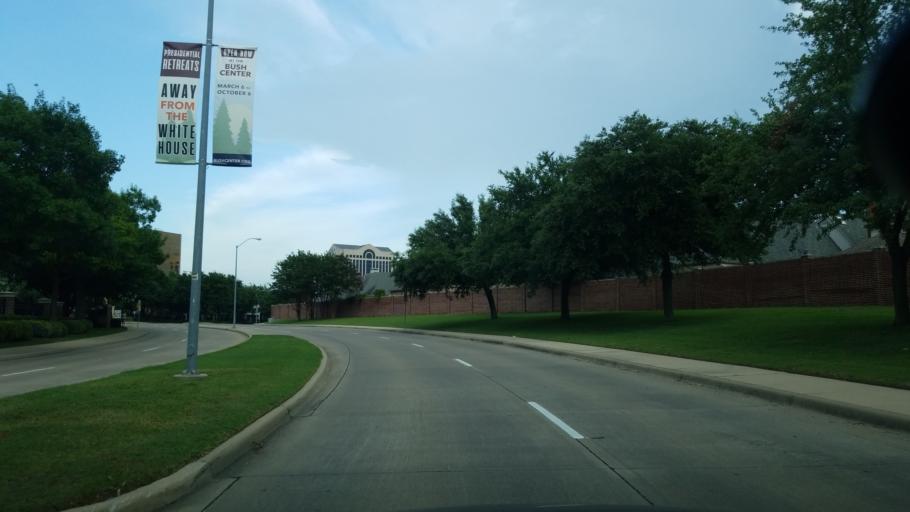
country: US
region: Texas
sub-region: Dallas County
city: University Park
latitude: 32.8628
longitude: -96.7755
